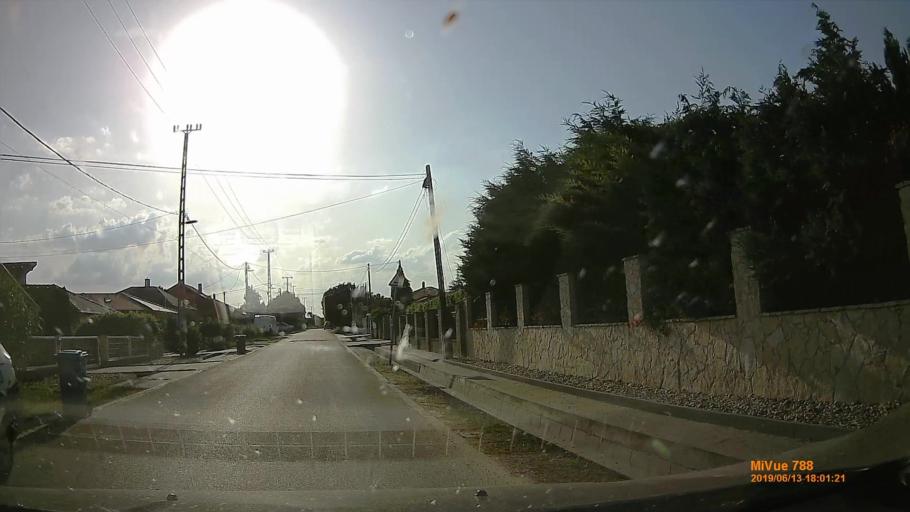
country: HU
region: Pest
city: Ecser
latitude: 47.4511
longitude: 19.3096
